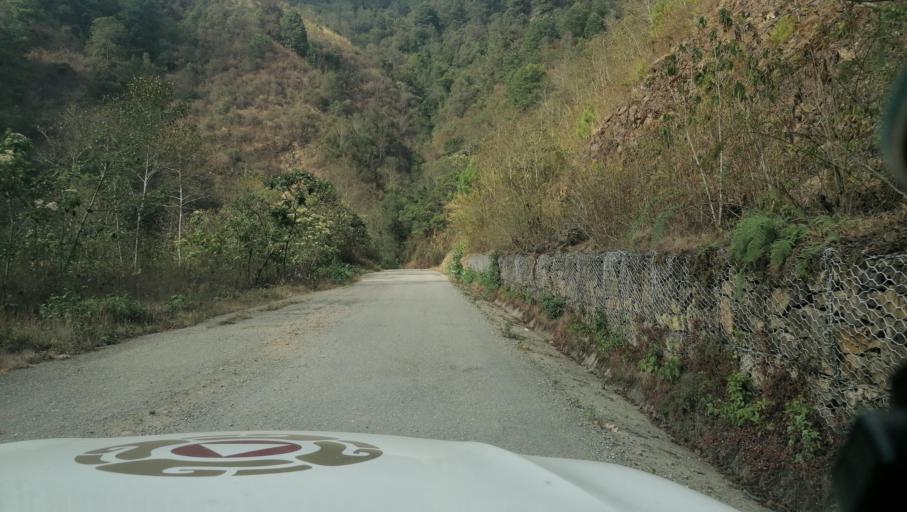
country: GT
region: San Marcos
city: Tacana
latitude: 15.2265
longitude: -92.1933
